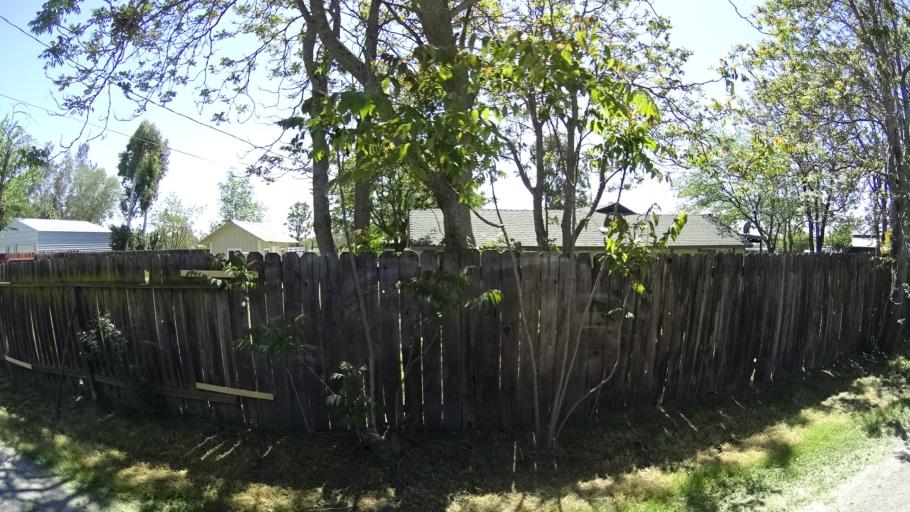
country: US
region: California
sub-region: Glenn County
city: Orland
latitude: 39.7354
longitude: -122.1925
